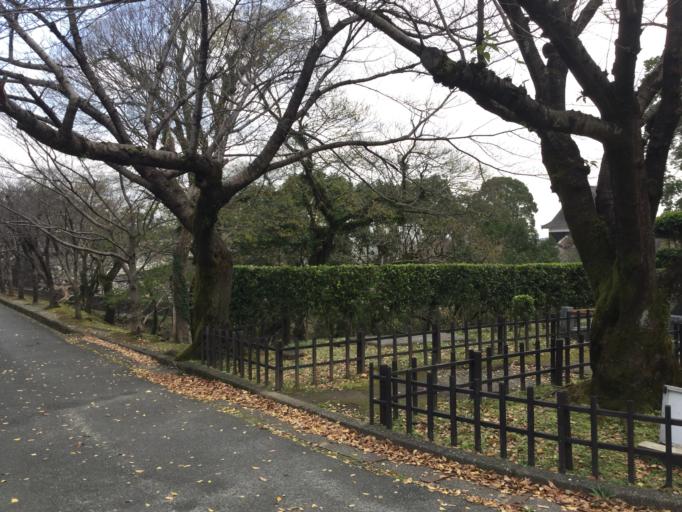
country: JP
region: Kumamoto
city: Kumamoto
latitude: 32.8058
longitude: 130.7025
